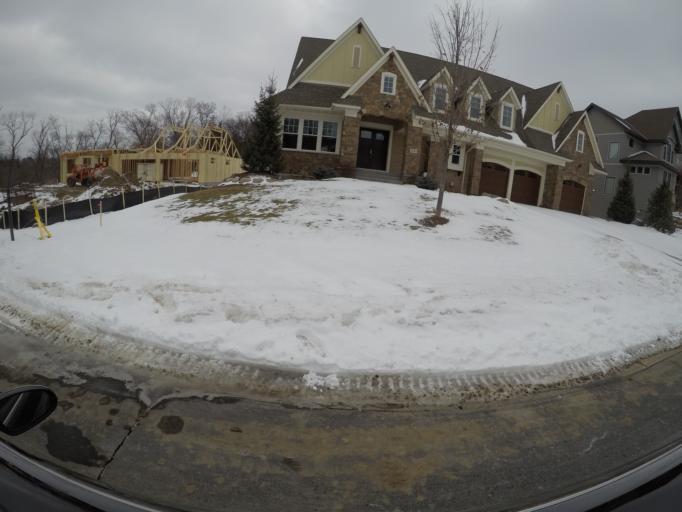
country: US
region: Minnesota
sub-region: Hennepin County
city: Eden Prairie
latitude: 44.8300
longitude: -93.4916
